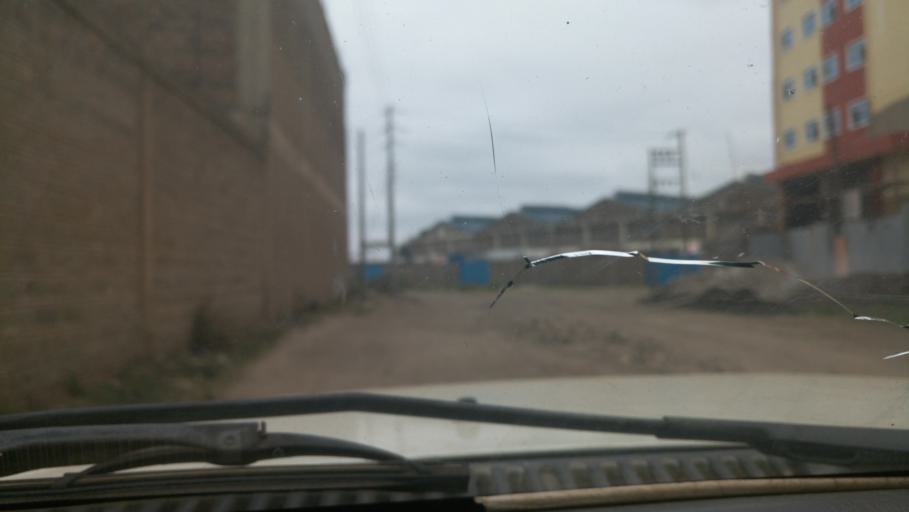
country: KE
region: Nairobi Area
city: Pumwani
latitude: -1.3352
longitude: 36.8679
